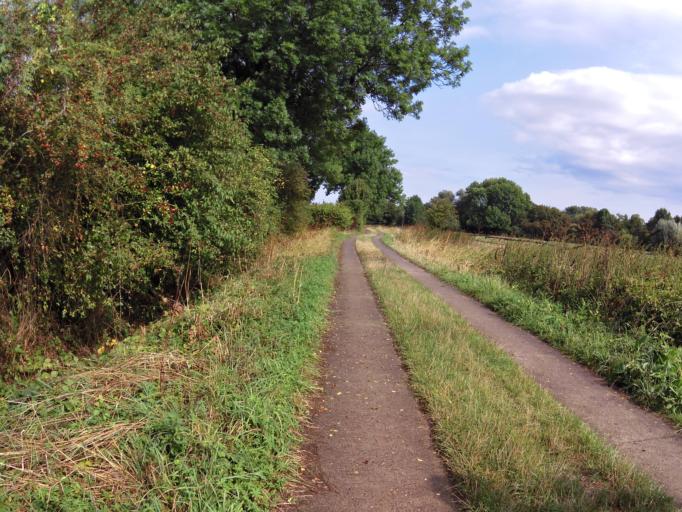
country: DE
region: Lower Saxony
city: Marklohe
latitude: 52.6611
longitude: 9.1802
